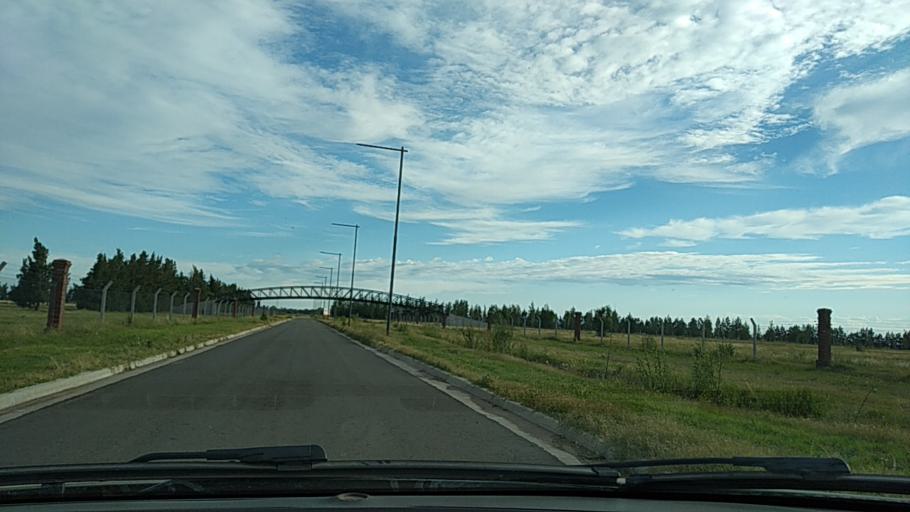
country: AR
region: Santa Fe
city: Funes
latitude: -32.9441
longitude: -60.7688
